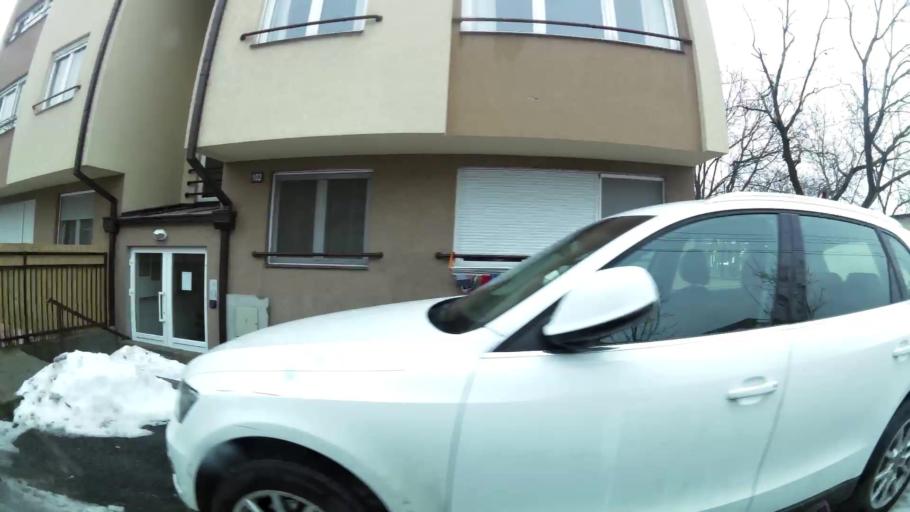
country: RS
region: Central Serbia
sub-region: Belgrade
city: Zemun
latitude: 44.8465
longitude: 20.3902
